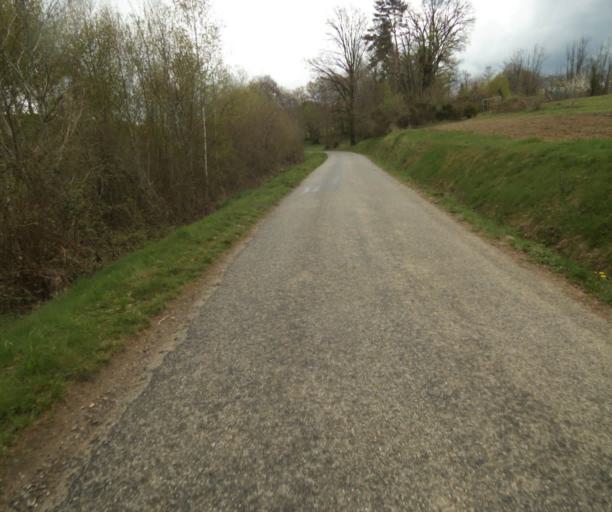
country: FR
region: Limousin
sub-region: Departement de la Correze
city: Laguenne
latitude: 45.2485
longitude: 1.8568
